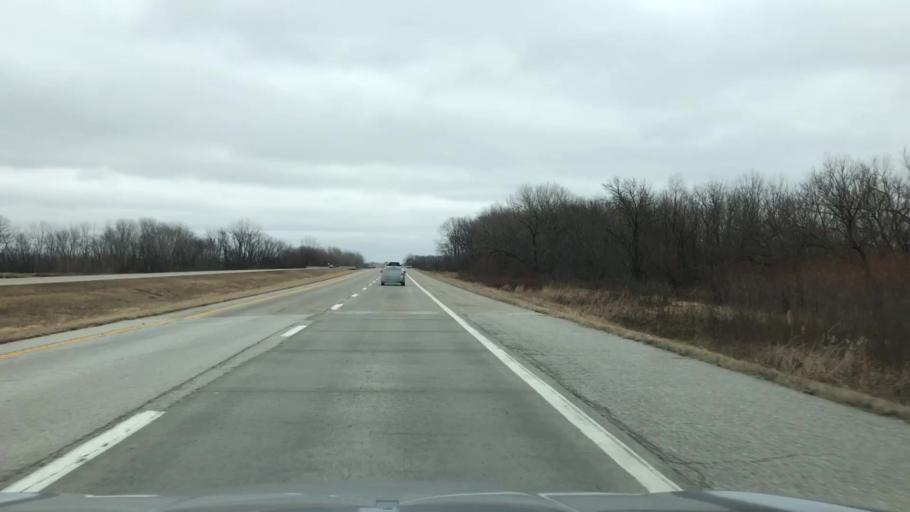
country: US
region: Missouri
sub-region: Livingston County
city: Chillicothe
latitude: 39.7766
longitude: -93.4296
